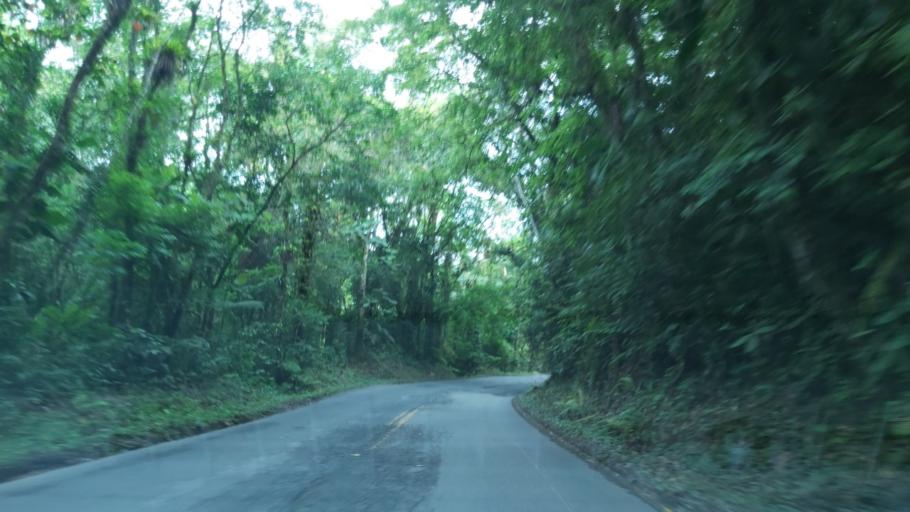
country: BR
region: Sao Paulo
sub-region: Juquia
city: Juquia
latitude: -24.0795
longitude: -47.6064
